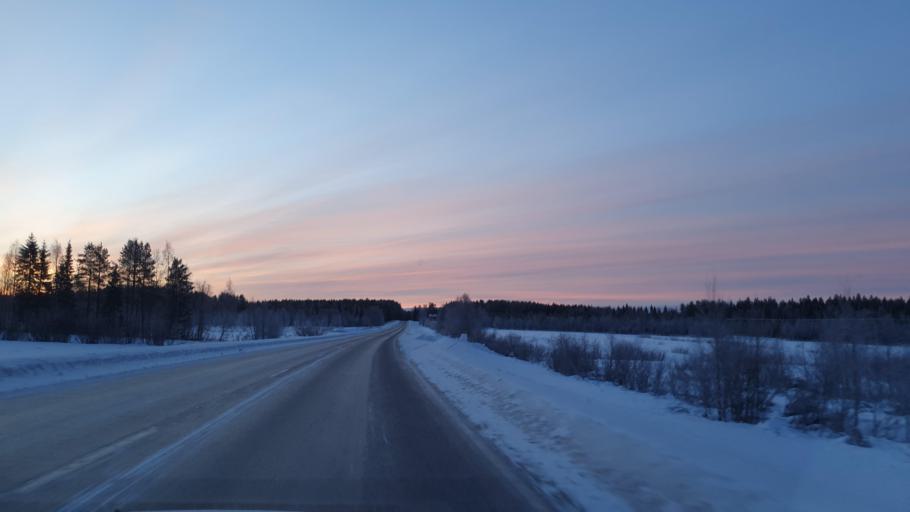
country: FI
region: Lapland
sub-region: Torniolaakso
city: Pello
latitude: 67.0214
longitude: 24.0442
